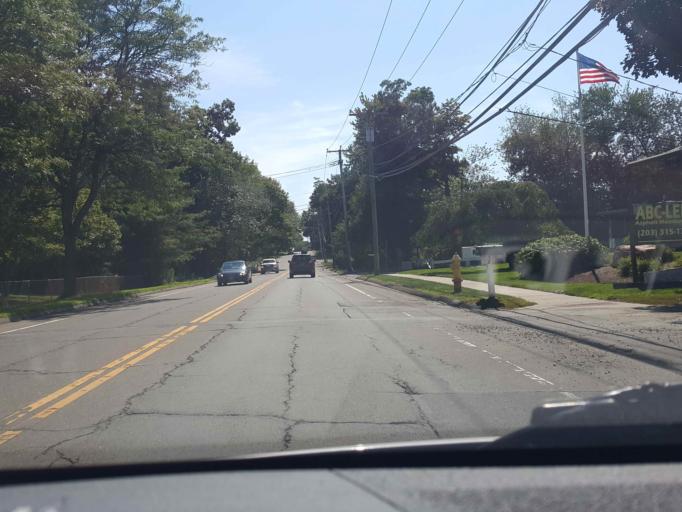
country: US
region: Connecticut
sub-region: New Haven County
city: North Branford
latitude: 41.3064
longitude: -72.7535
